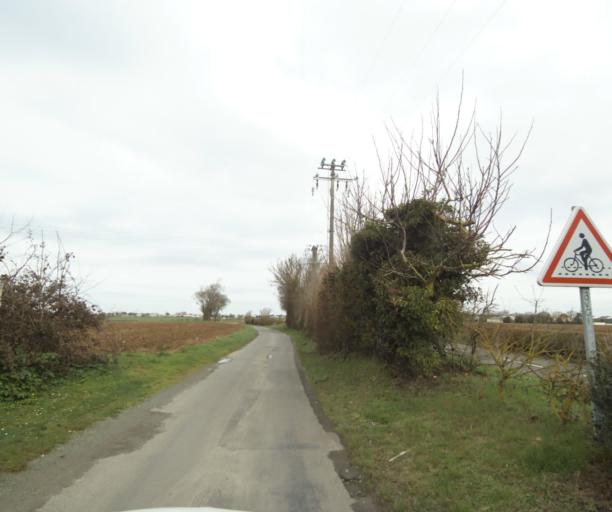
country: FR
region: Poitou-Charentes
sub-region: Departement de la Charente-Maritime
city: Lagord
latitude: 46.1916
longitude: -1.1666
